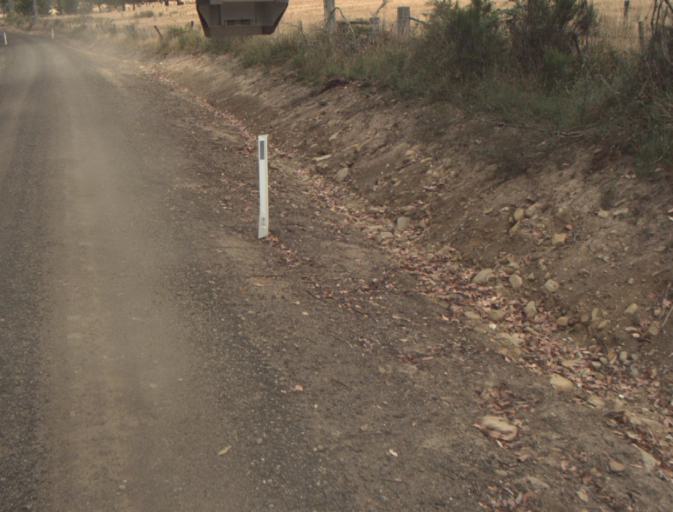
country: AU
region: Tasmania
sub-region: Northern Midlands
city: Evandale
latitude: -41.4584
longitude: 147.4465
